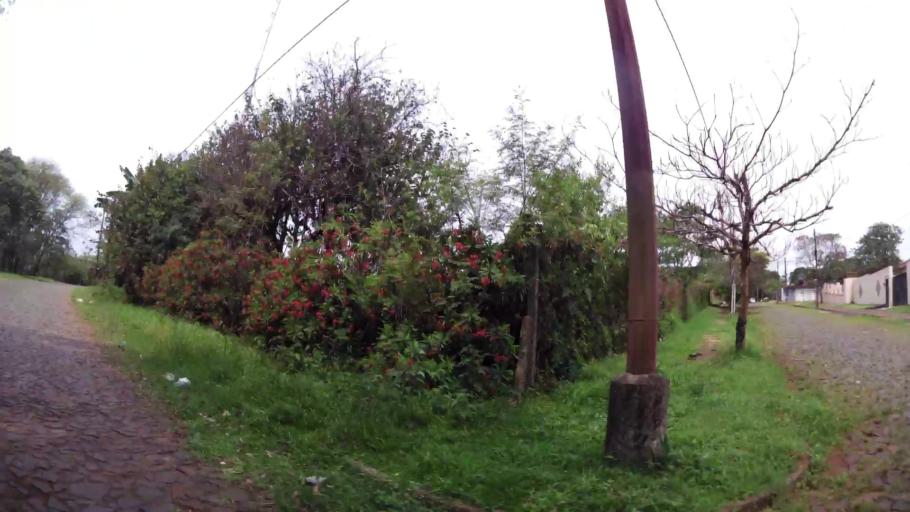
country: PY
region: Alto Parana
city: Presidente Franco
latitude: -25.5492
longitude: -54.6147
